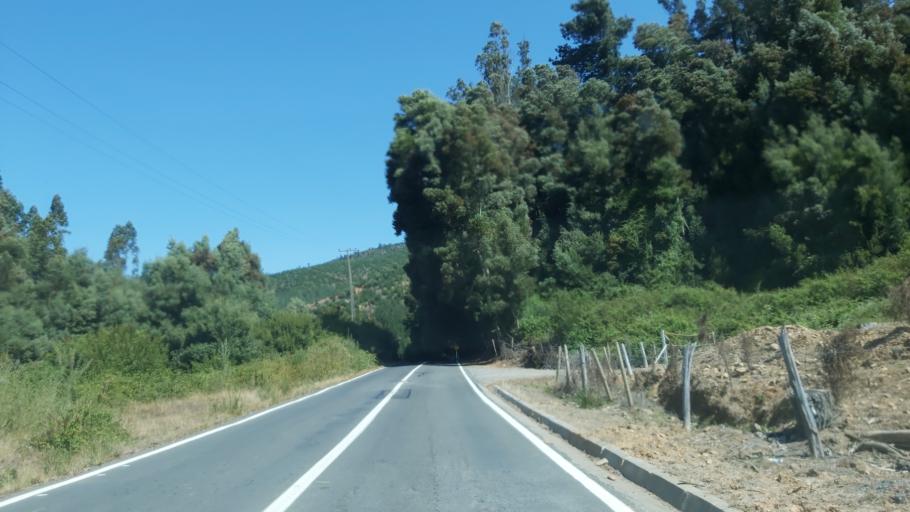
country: CL
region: Biobio
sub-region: Provincia de Concepcion
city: Tome
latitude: -36.5512
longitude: -72.8787
